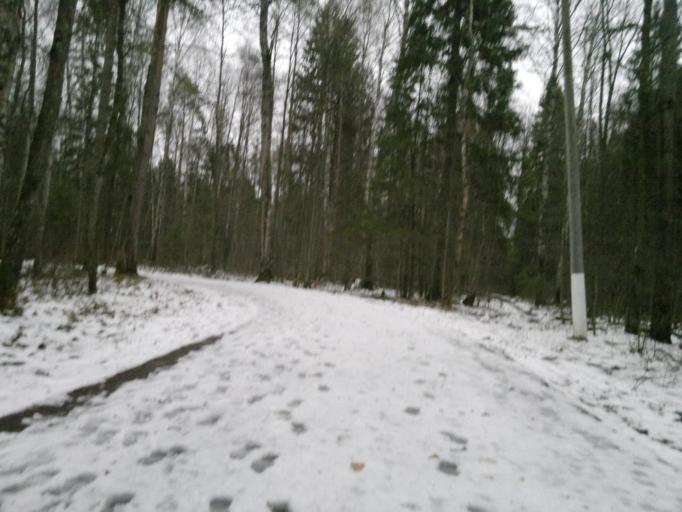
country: RU
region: Mariy-El
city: Yoshkar-Ola
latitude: 56.6024
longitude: 47.9619
